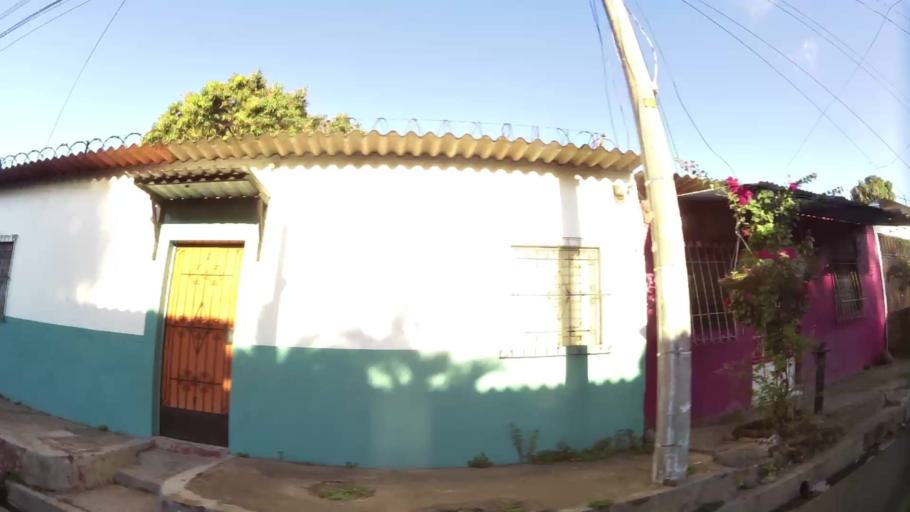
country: SV
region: Sonsonate
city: San Antonio del Monte
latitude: 13.7093
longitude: -89.7329
